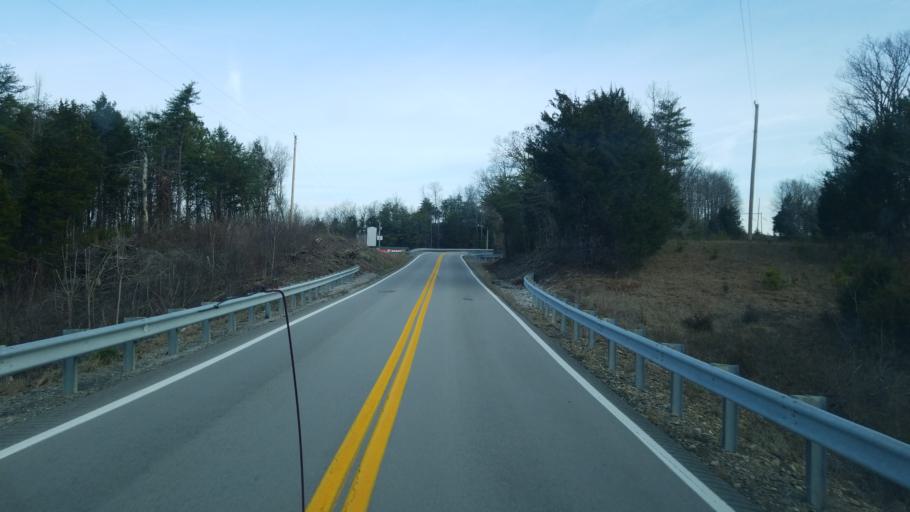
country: US
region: Kentucky
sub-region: Clinton County
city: Albany
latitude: 36.8510
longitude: -85.1617
